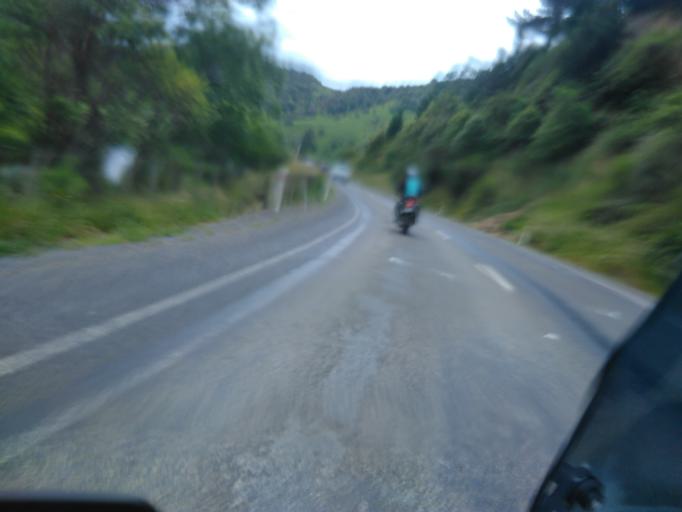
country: NZ
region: Bay of Plenty
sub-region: Opotiki District
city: Opotiki
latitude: -38.3772
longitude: 177.4822
